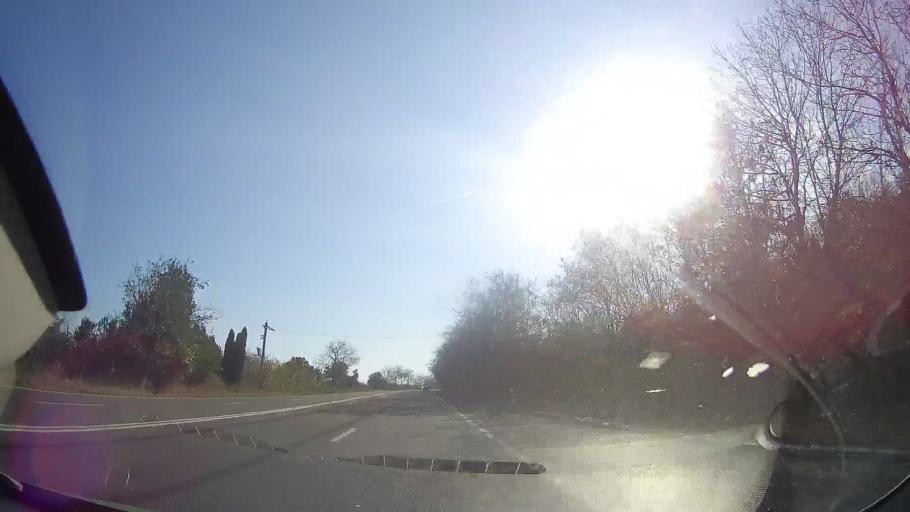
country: RO
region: Constanta
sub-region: Comuna Douazeci si Trei August
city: Dulcesti
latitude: 43.8882
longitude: 28.5729
